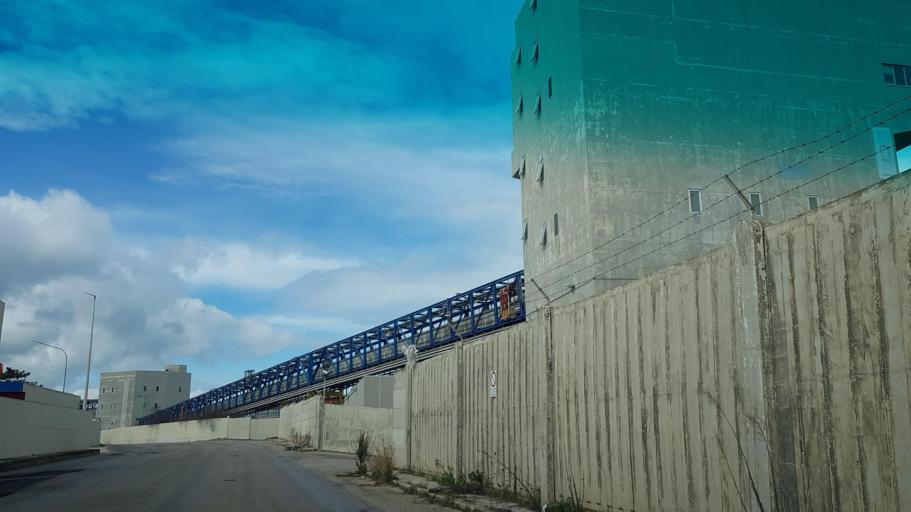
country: IT
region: Apulia
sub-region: Provincia di Brindisi
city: Materdomini
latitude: 40.6452
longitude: 17.9803
